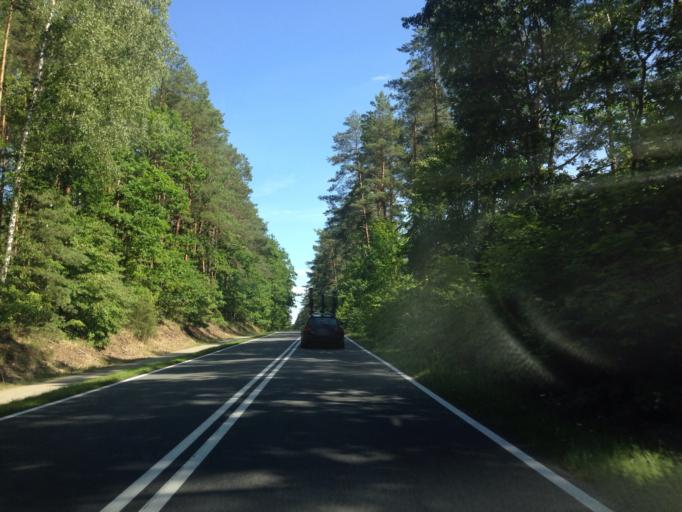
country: PL
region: Kujawsko-Pomorskie
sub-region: Powiat swiecki
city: Osie
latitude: 53.6085
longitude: 18.3080
